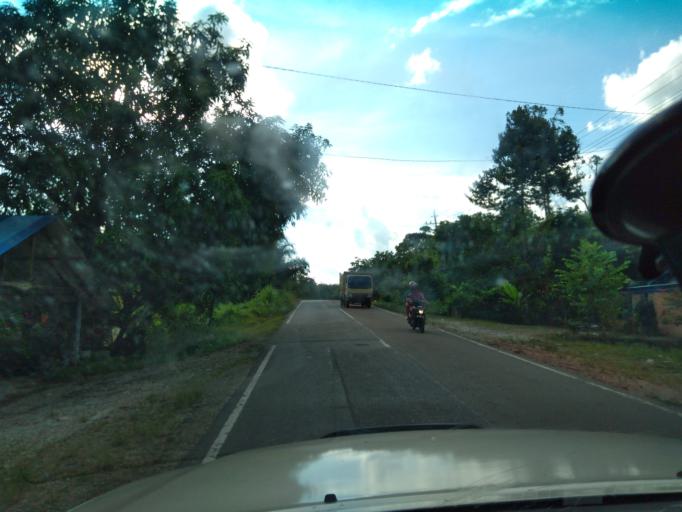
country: ID
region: West Kalimantan
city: Tayan
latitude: 0.3664
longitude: 109.9896
